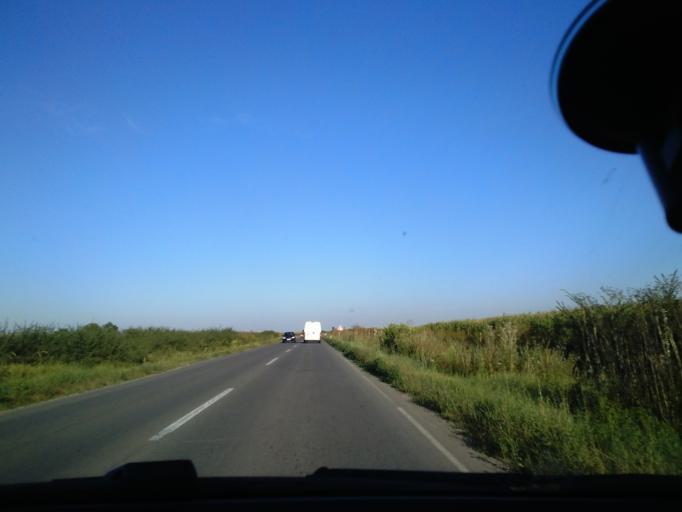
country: RS
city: Maglic
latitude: 45.4045
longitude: 19.4303
